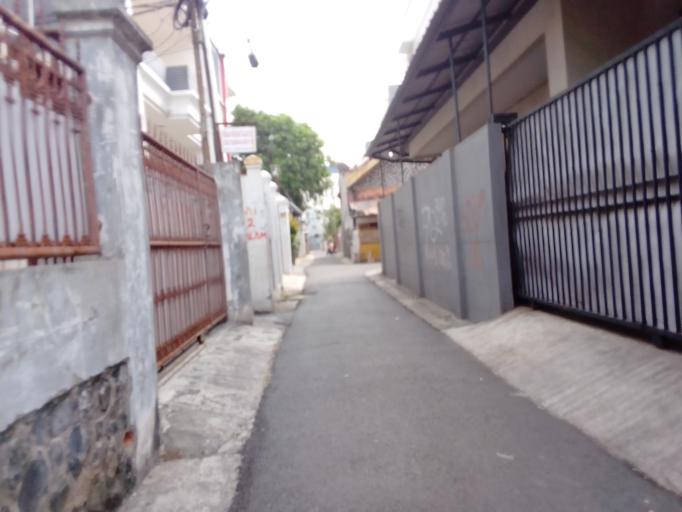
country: ID
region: Jakarta Raya
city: Jakarta
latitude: -6.1692
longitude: 106.8075
